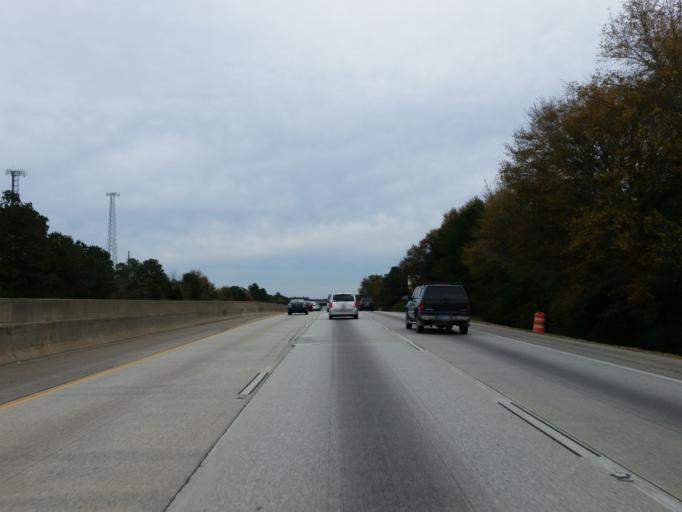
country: US
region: Georgia
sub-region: Monroe County
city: Forsyth
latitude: 33.0137
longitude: -83.8834
